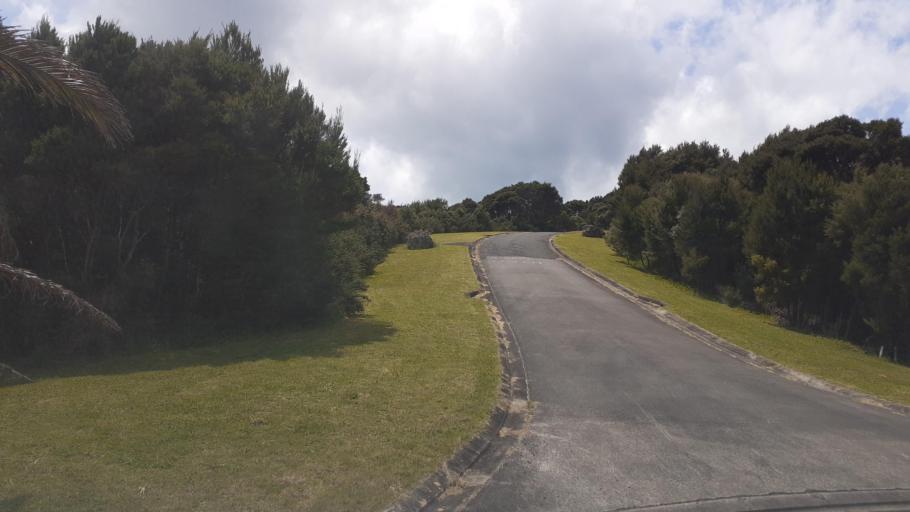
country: NZ
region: Northland
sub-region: Far North District
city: Paihia
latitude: -35.2762
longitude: 174.1436
